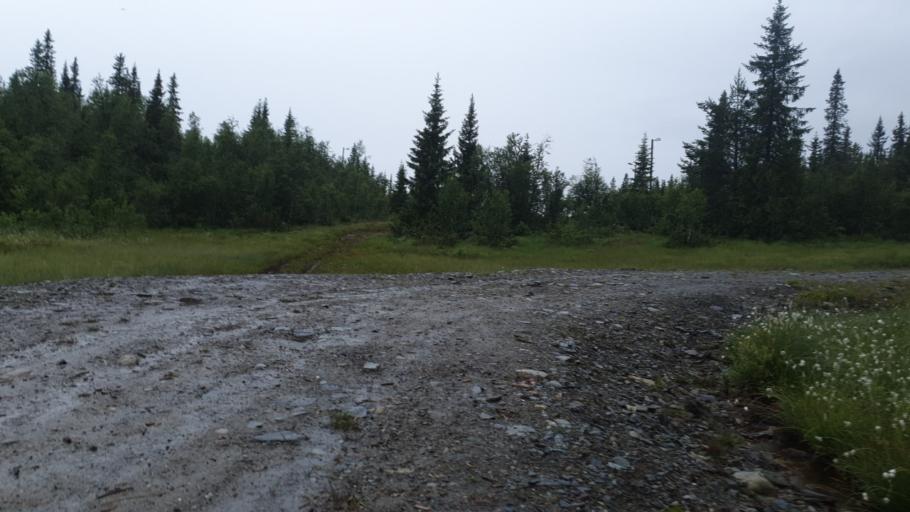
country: NO
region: Oppland
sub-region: Vestre Slidre
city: Slidre
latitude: 61.2332
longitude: 8.9170
